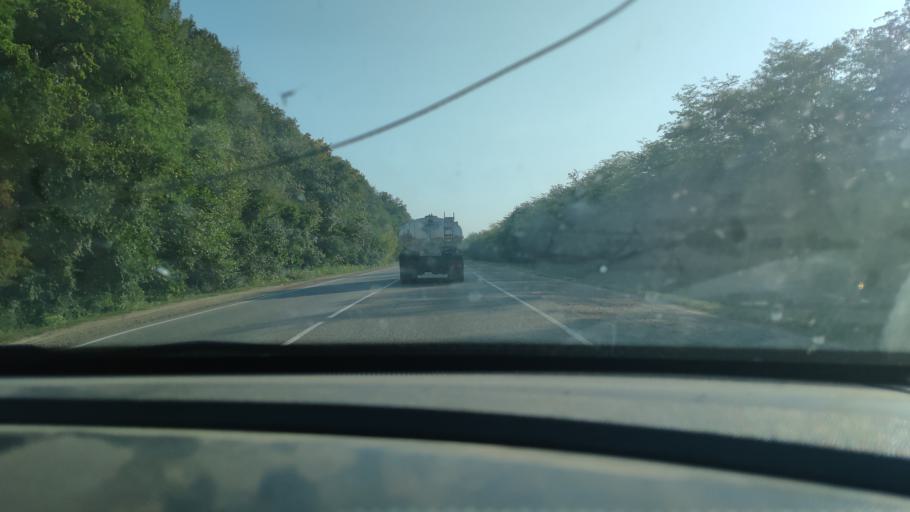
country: RU
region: Krasnodarskiy
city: Starominskaya
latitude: 46.4892
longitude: 39.0575
